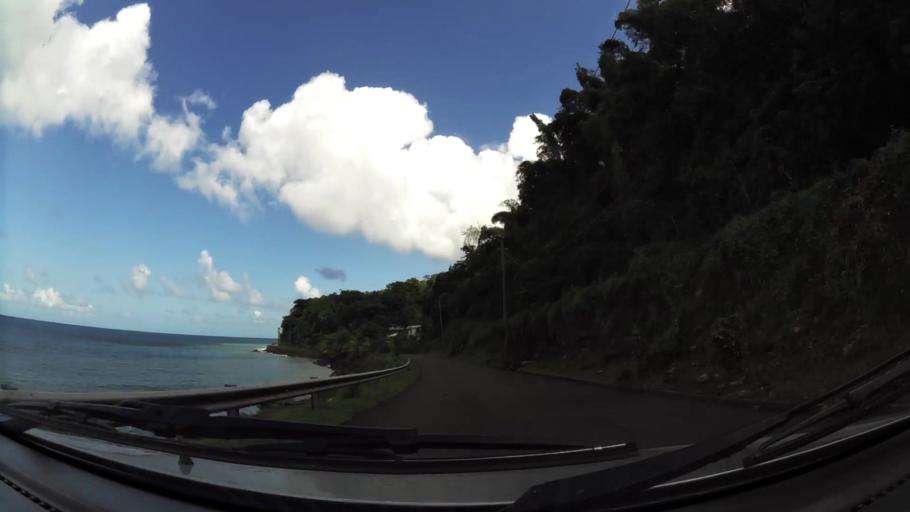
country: GD
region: Saint Mark
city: Victoria
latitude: 12.1866
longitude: -61.7196
